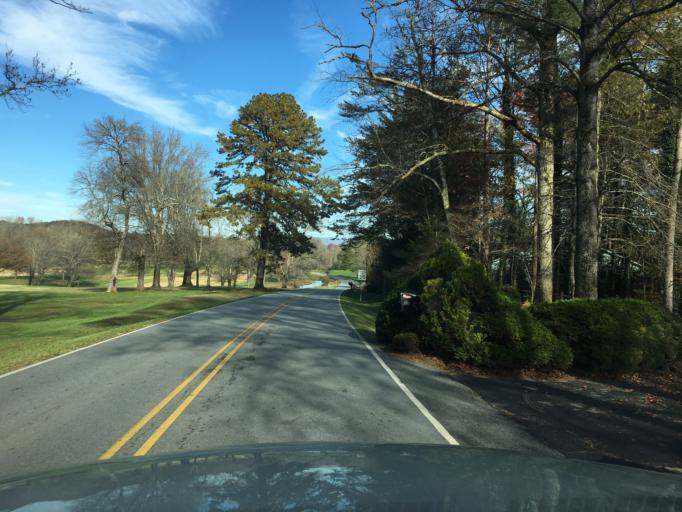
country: US
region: North Carolina
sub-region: Henderson County
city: Etowah
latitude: 35.3211
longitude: -82.6090
